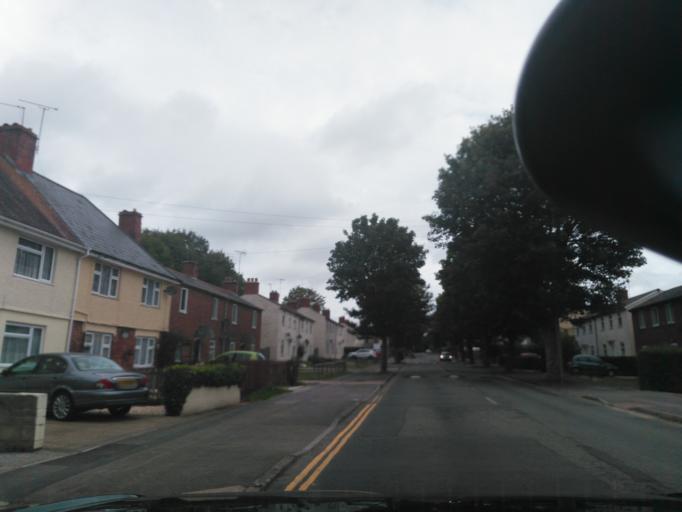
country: GB
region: England
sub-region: Borough of Swindon
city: Swindon
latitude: 51.5777
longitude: -1.7849
